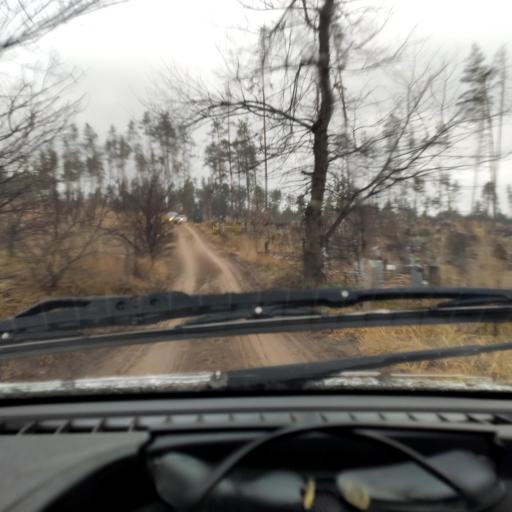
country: RU
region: Samara
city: Zhigulevsk
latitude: 53.5364
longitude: 49.5547
